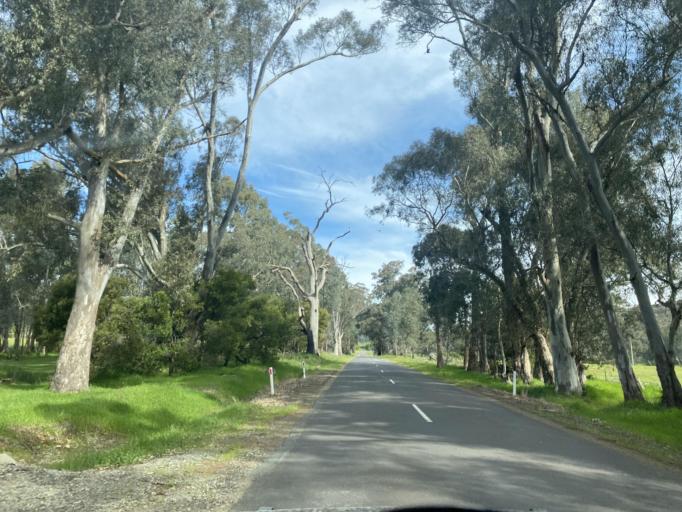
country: AU
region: Victoria
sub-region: Benalla
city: Benalla
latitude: -36.7795
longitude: 146.1379
